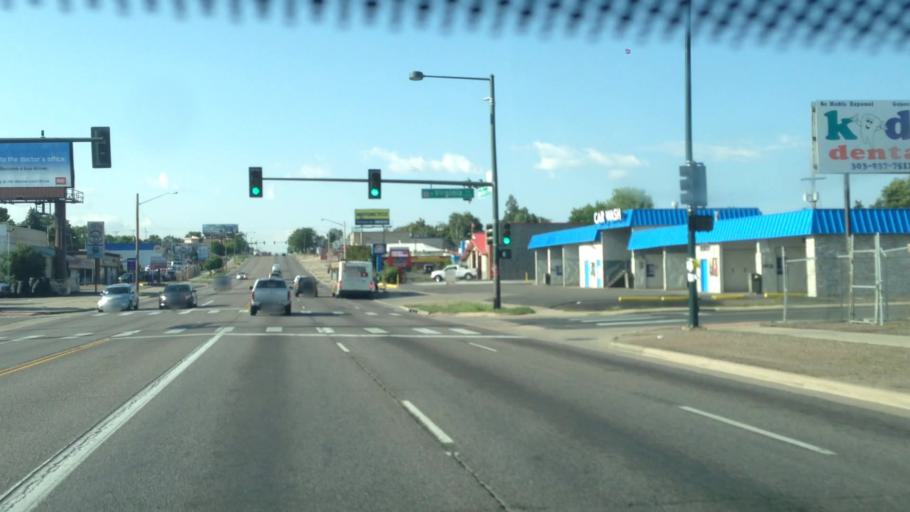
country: US
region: Colorado
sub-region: Denver County
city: Denver
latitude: 39.7079
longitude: -105.0253
